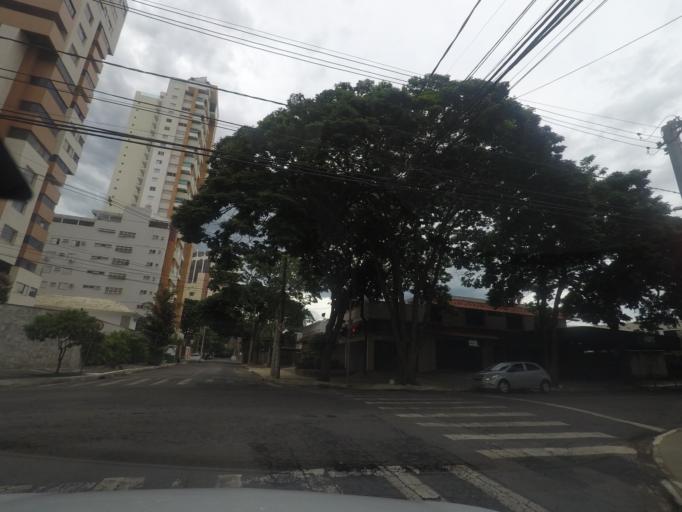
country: BR
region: Goias
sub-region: Goiania
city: Goiania
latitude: -16.6868
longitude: -49.2631
